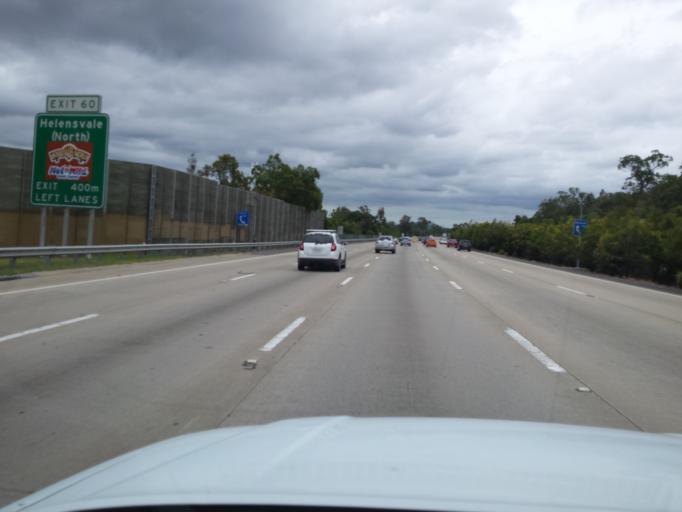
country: AU
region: Queensland
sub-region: Gold Coast
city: Upper Coomera
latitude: -27.9171
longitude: 153.3210
